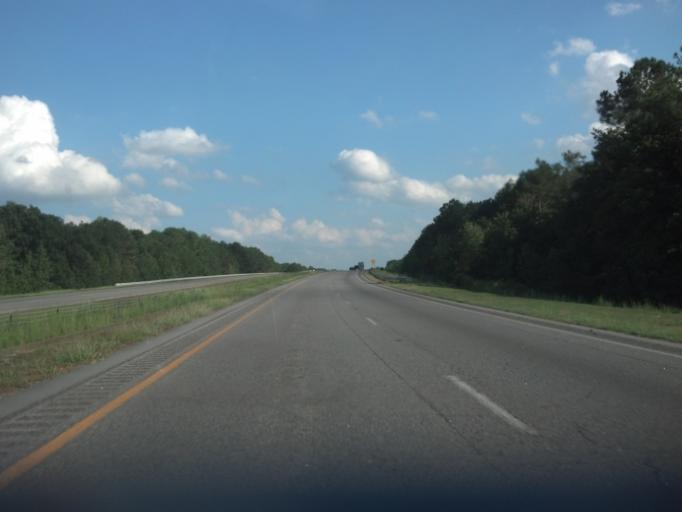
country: US
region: North Carolina
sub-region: Edgecombe County
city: Tarboro
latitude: 35.9205
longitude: -77.6597
